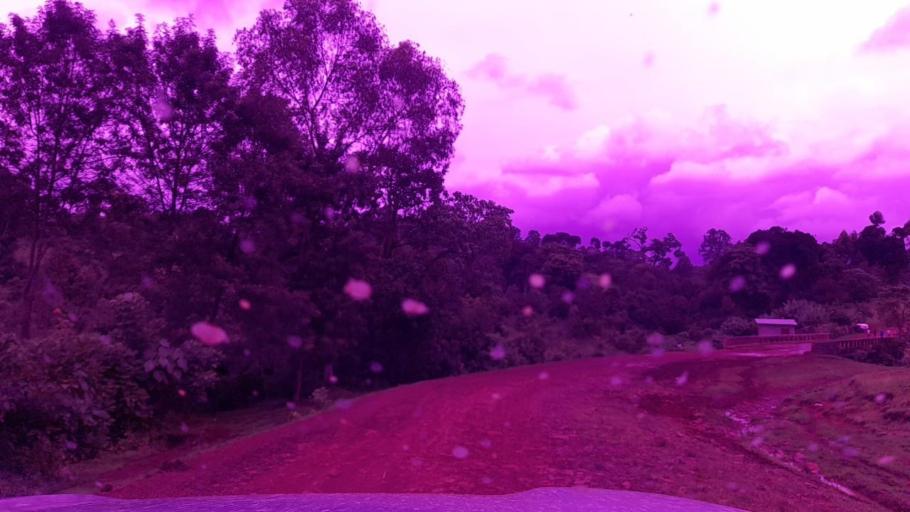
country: ET
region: Southern Nations, Nationalities, and People's Region
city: Tippi
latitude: 7.5757
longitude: 35.6647
